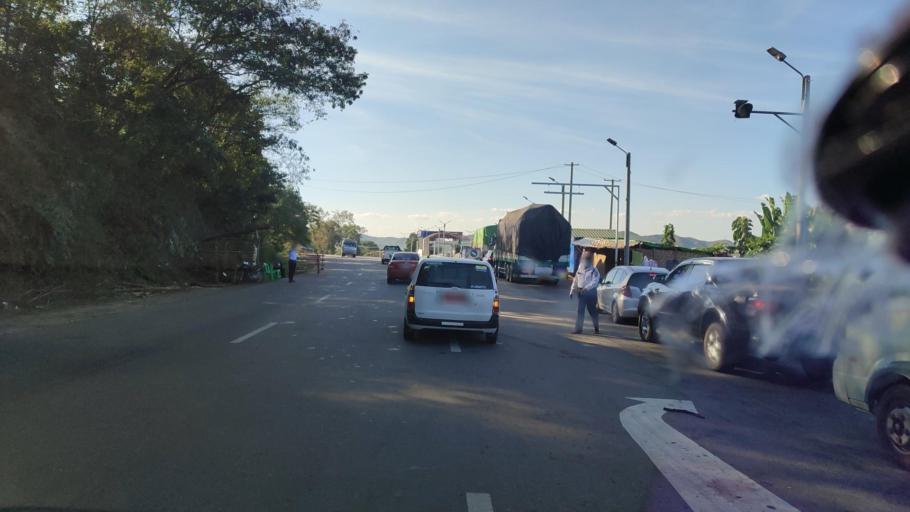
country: MM
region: Mandalay
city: Yamethin
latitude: 20.7507
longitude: 96.2751
